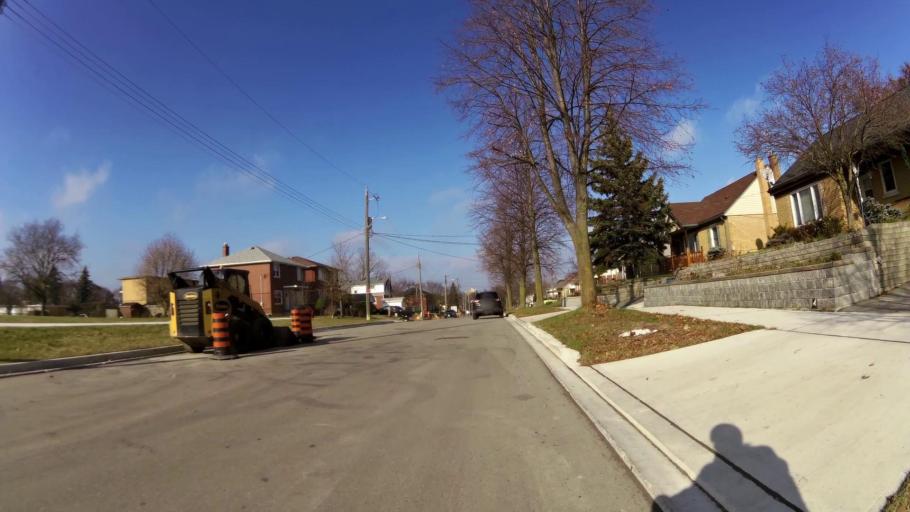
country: CA
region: Ontario
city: Kitchener
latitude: 43.4304
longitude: -80.4842
